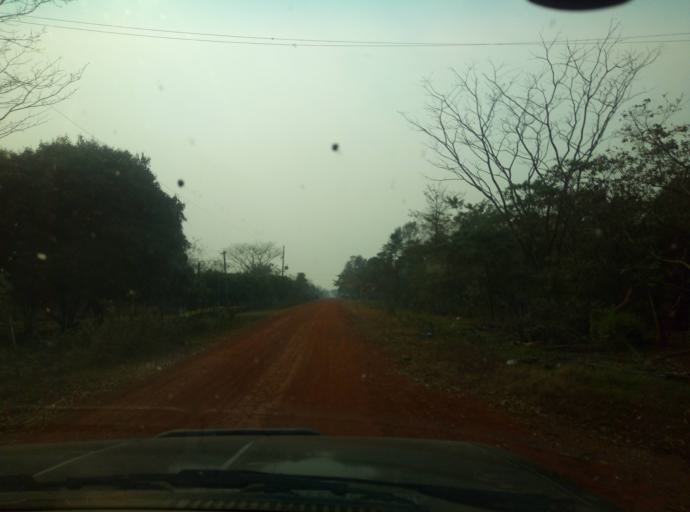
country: PY
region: Caaguazu
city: Carayao
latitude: -25.2042
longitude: -56.2470
